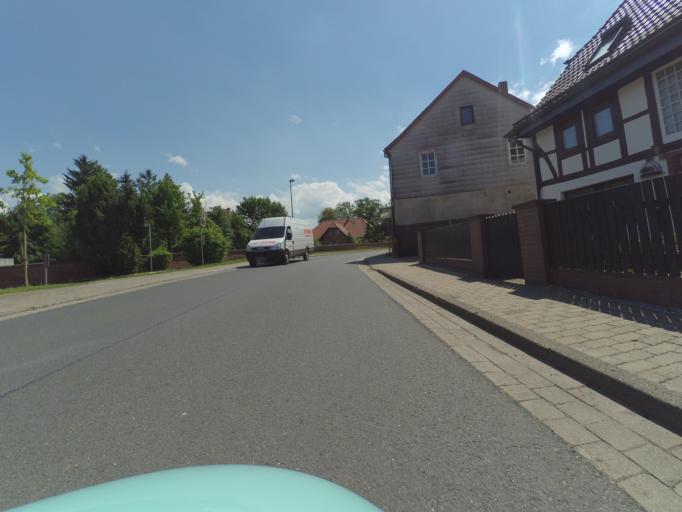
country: DE
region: Lower Saxony
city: Hohenhameln
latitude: 52.2192
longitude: 10.0349
